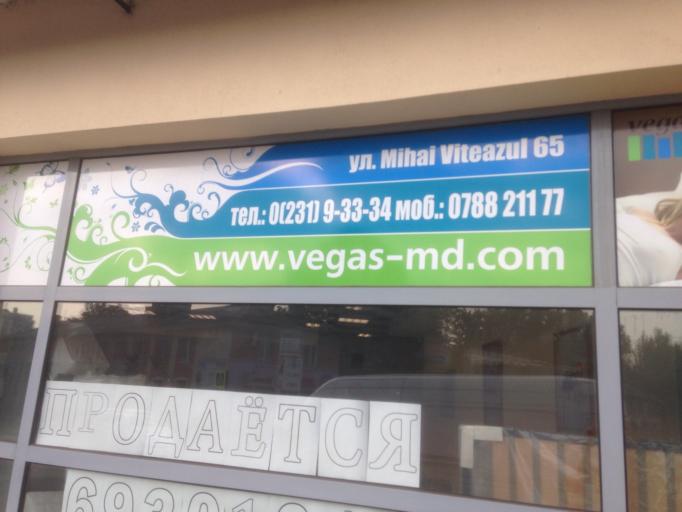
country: MD
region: Balti
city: Balti
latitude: 47.7648
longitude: 27.9323
